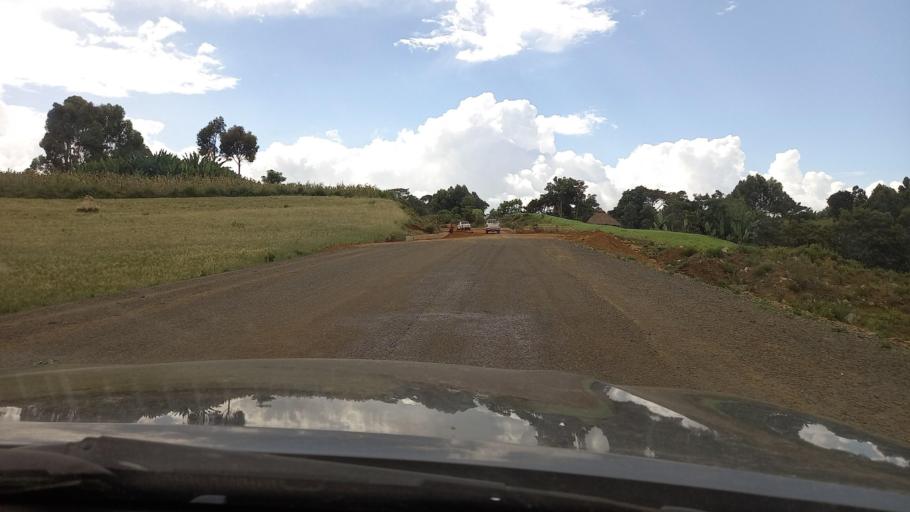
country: ET
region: Southern Nations, Nationalities, and People's Region
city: Mizan Teferi
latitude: 6.2177
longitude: 35.6361
